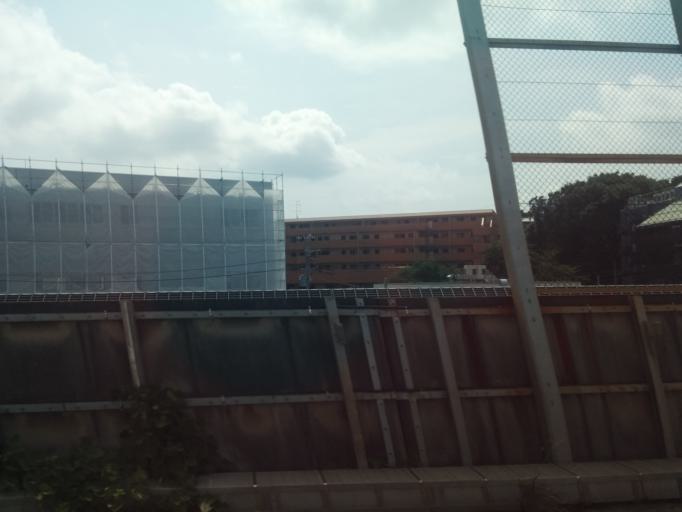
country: JP
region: Kanagawa
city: Yokohama
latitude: 35.4977
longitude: 139.6058
